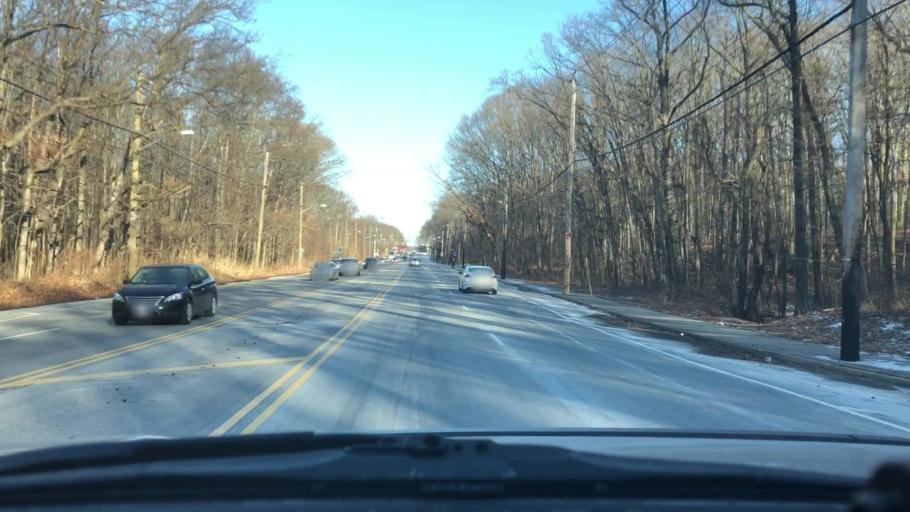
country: US
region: New York
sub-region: Richmond County
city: Staten Island
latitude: 40.5218
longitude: -74.1920
